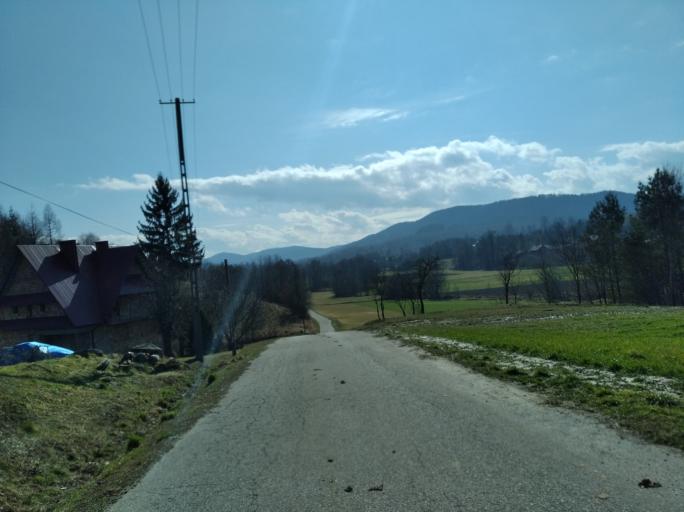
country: PL
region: Subcarpathian Voivodeship
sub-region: Powiat strzyzowski
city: Wysoka Strzyzowska
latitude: 49.8148
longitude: 21.7455
